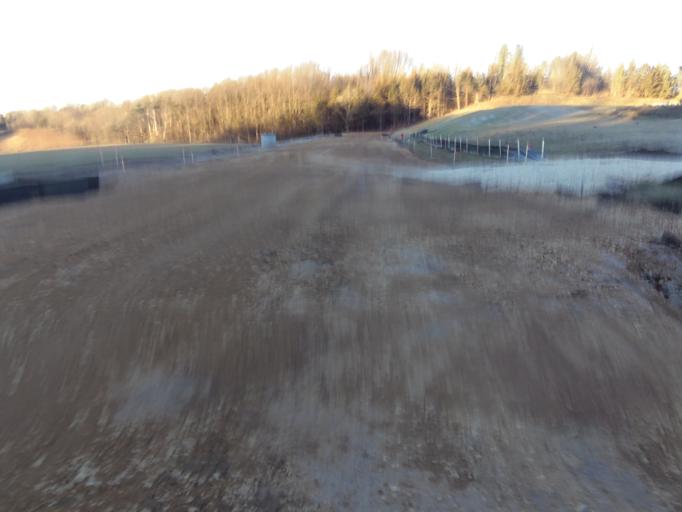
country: US
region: Wisconsin
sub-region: Saint Croix County
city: Hudson
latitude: 44.9694
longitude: -92.7230
